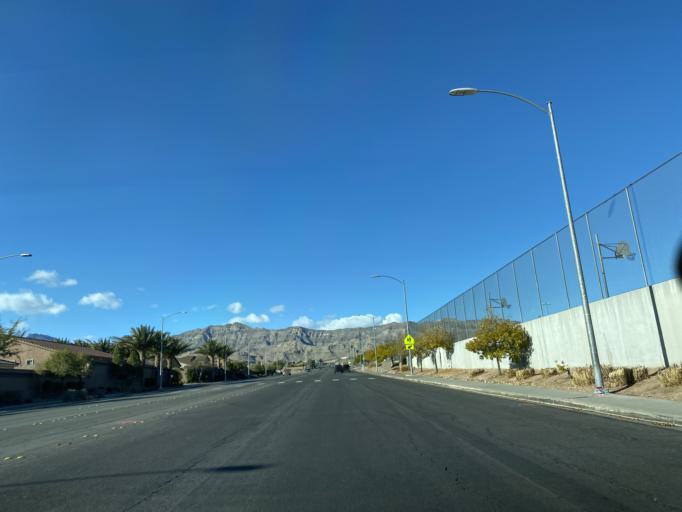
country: US
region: Nevada
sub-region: Clark County
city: Summerlin South
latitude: 36.2774
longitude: -115.3167
